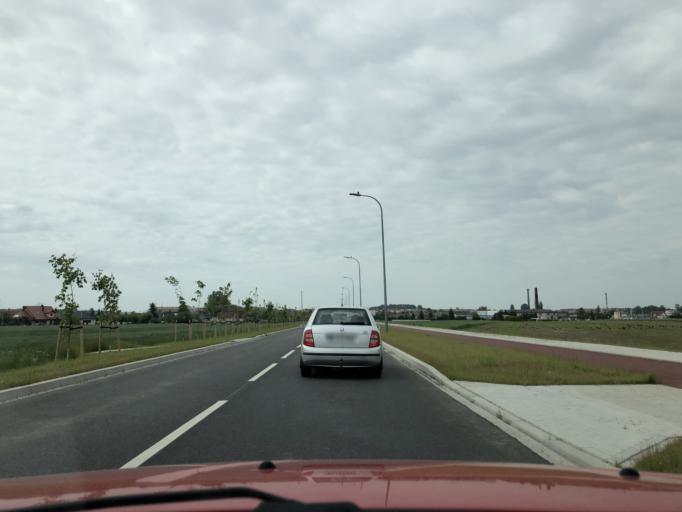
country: PL
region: Greater Poland Voivodeship
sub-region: Powiat jarocinski
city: Jarocin
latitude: 51.9726
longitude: 17.5207
